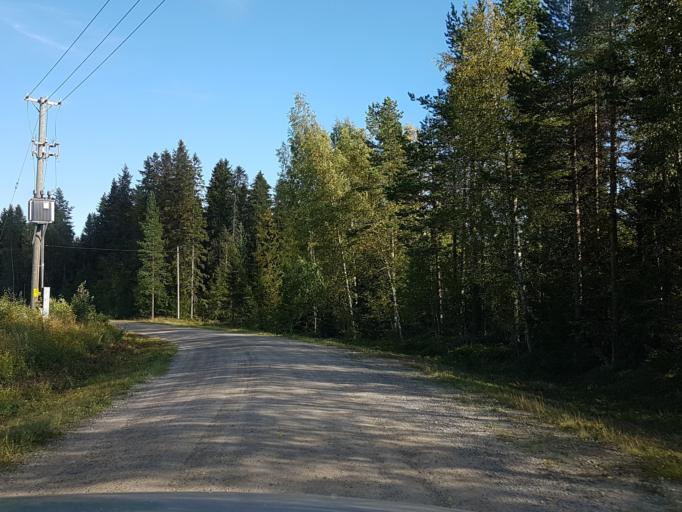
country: SE
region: Vaesterbotten
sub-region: Robertsfors Kommun
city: Robertsfors
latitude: 64.0497
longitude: 20.8734
